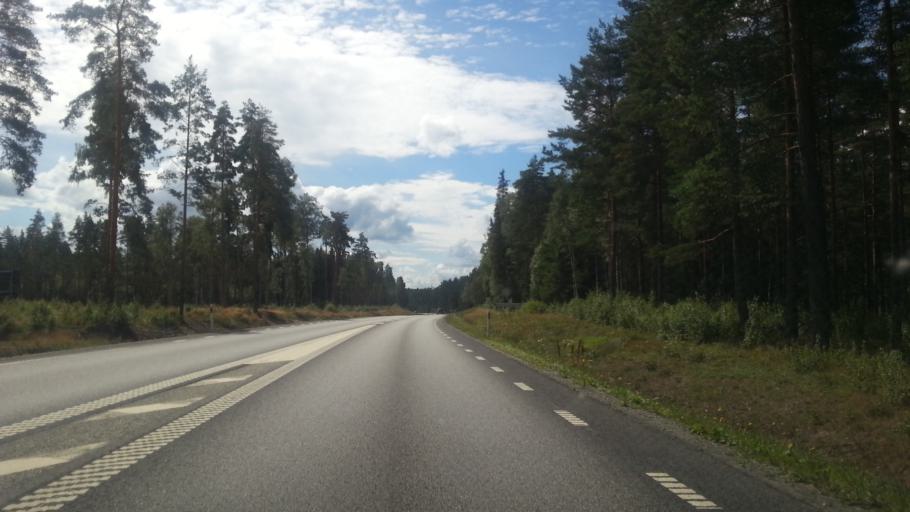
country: SE
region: OErebro
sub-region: Lindesbergs Kommun
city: Lindesberg
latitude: 59.6161
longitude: 15.1883
